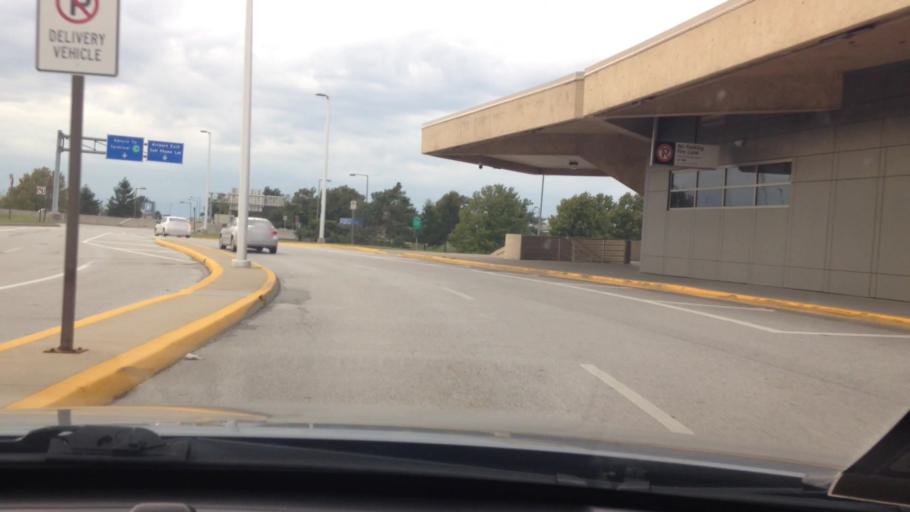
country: US
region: Missouri
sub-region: Platte County
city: Weatherby Lake
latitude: 39.2952
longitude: -94.7127
